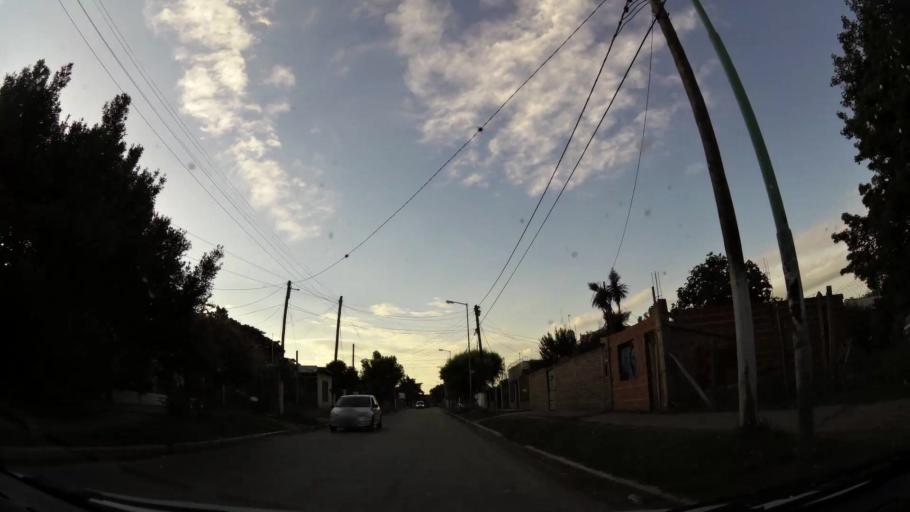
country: AR
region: Buenos Aires
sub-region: Partido de Merlo
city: Merlo
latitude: -34.6856
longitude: -58.7552
